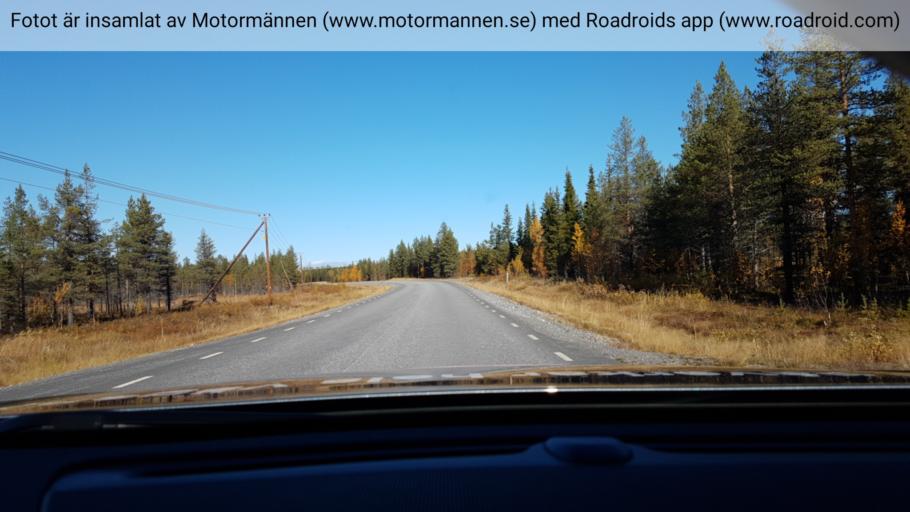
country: SE
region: Norrbotten
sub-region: Gallivare Kommun
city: Gaellivare
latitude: 66.8171
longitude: 21.0428
